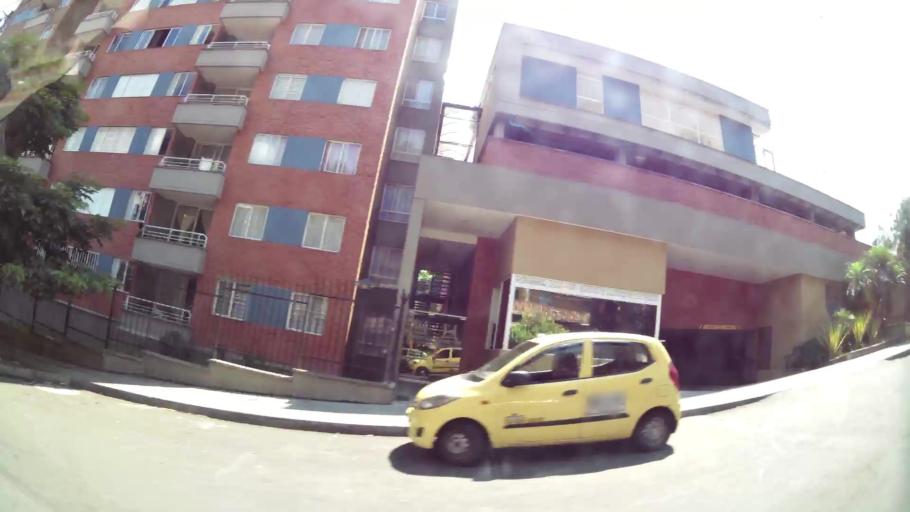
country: CO
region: Antioquia
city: Itagui
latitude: 6.2047
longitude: -75.5994
